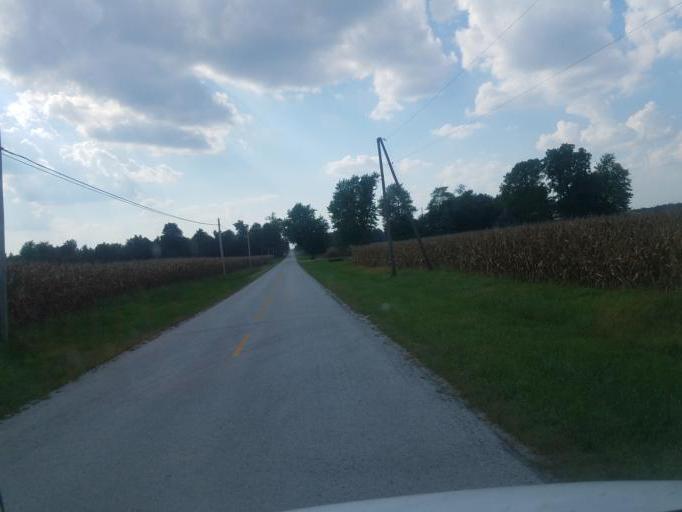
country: US
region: Ohio
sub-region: Hancock County
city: Arlington
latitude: 40.7906
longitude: -83.6755
